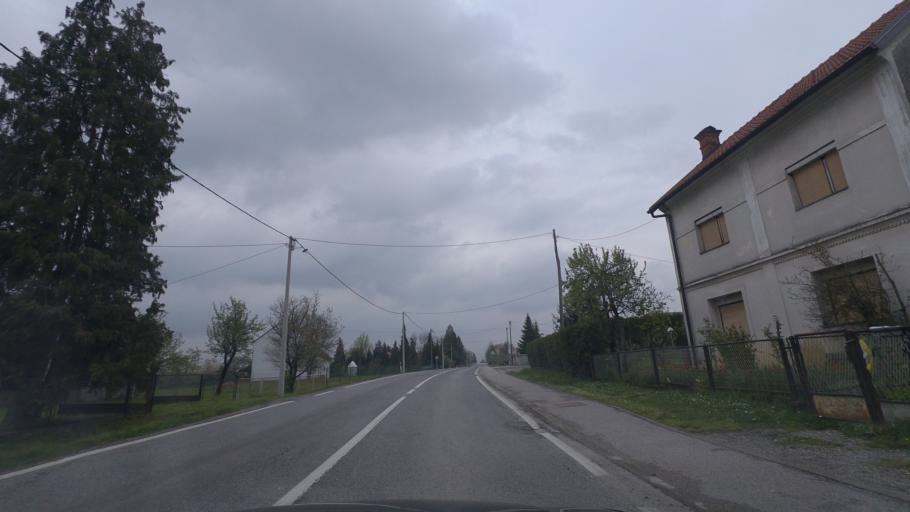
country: HR
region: Zagrebacka
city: Jastrebarsko
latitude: 45.5985
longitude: 15.5987
